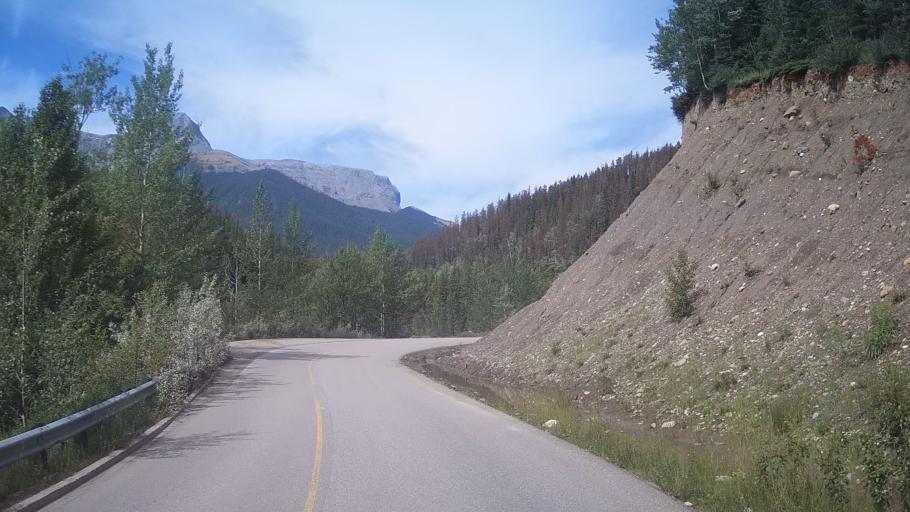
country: CA
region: Alberta
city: Hinton
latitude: 53.1775
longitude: -117.8451
